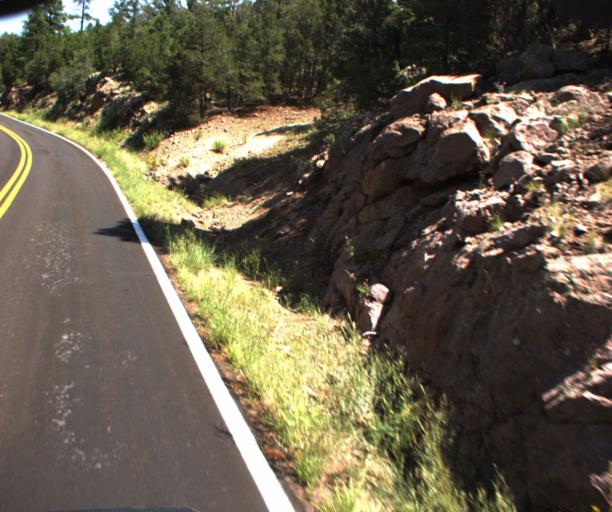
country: US
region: Arizona
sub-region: Greenlee County
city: Morenci
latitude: 33.3998
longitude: -109.3375
